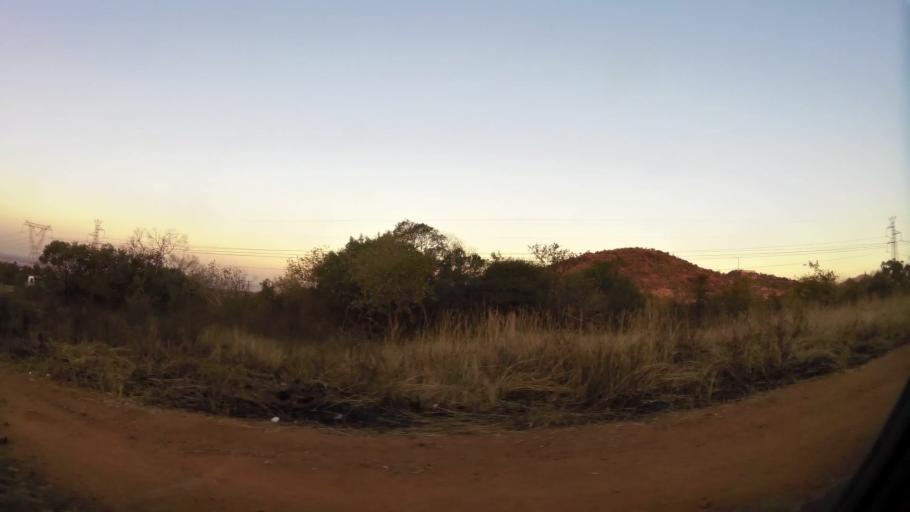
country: ZA
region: North-West
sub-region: Bojanala Platinum District Municipality
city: Rustenburg
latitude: -25.6079
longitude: 27.1795
